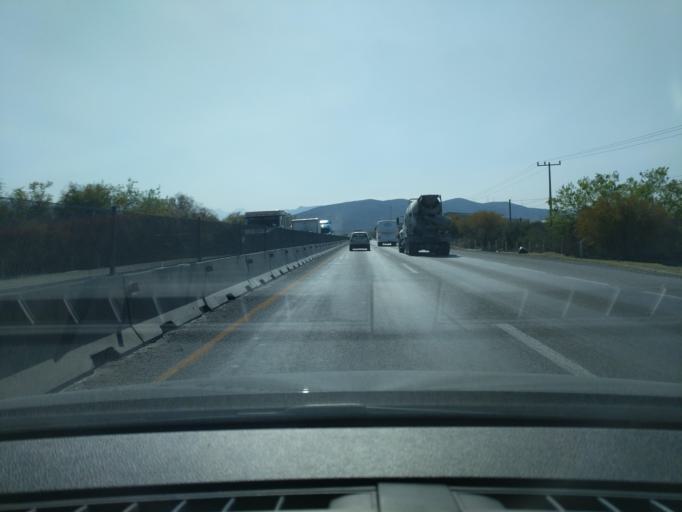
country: MX
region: Nuevo Leon
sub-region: Garcia
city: Los Parques
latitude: 25.7706
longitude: -100.4761
